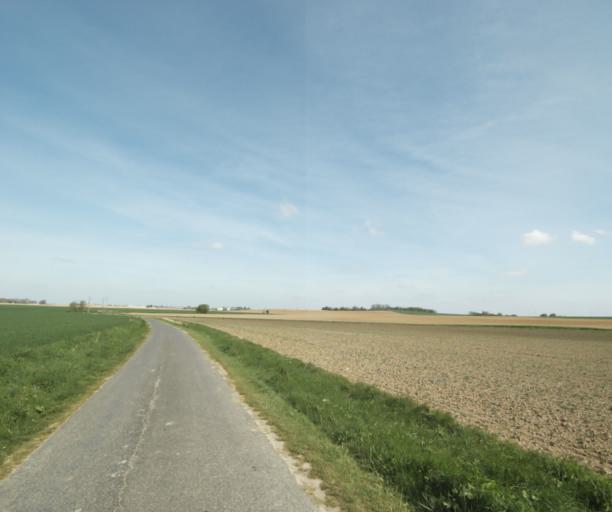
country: FR
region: Ile-de-France
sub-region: Departement de Seine-et-Marne
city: Nangis
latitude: 48.5439
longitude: 3.0366
